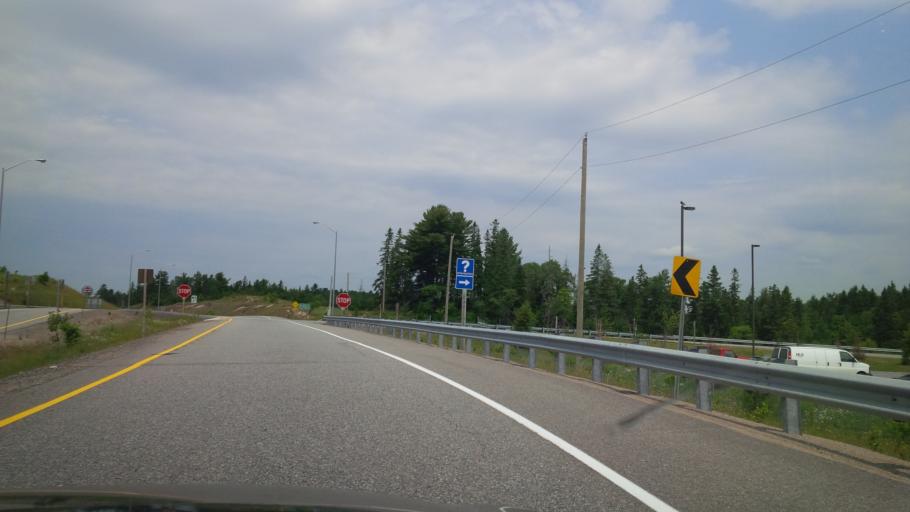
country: CA
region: Ontario
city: Huntsville
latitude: 45.5116
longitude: -79.3039
